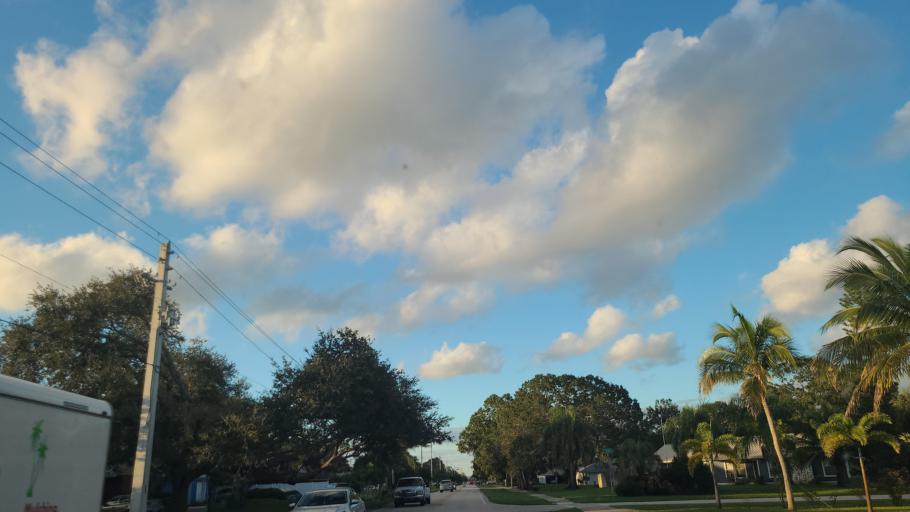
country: US
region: Florida
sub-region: Indian River County
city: Vero Beach South
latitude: 27.6023
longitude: -80.4059
